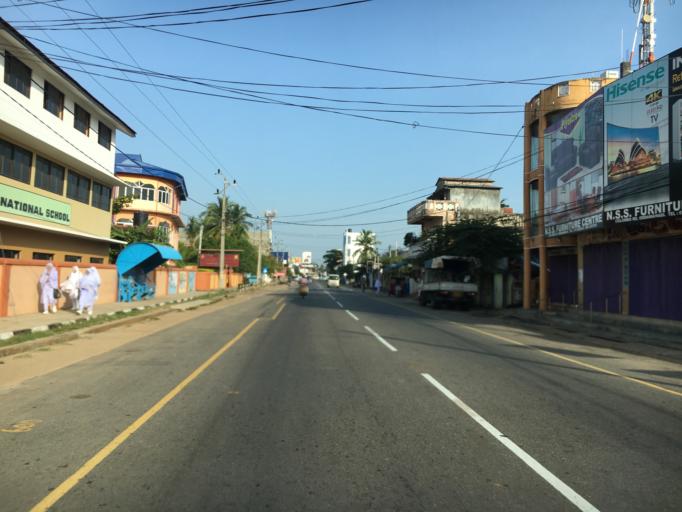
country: LK
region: Eastern Province
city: Eravur Town
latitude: 7.9133
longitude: 81.5251
